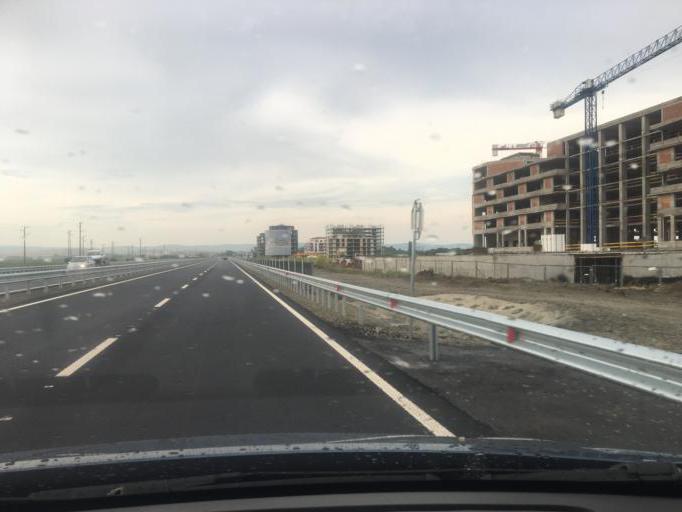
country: BG
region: Burgas
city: Aheloy
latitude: 42.6265
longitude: 27.6311
